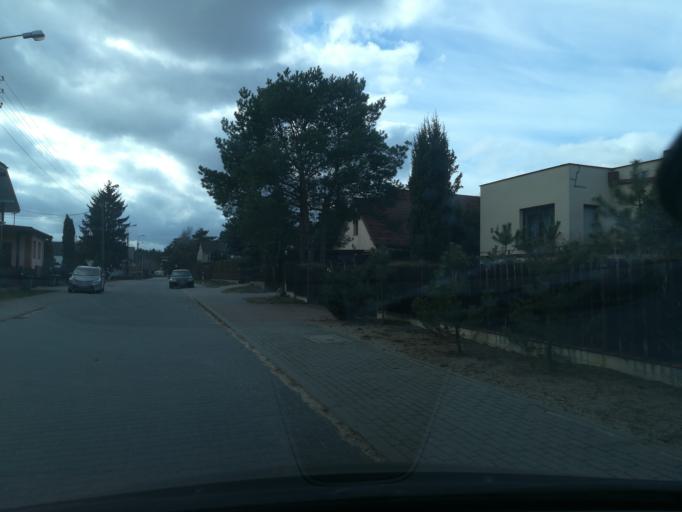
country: PL
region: Kujawsko-Pomorskie
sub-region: Powiat torunski
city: Lubicz Dolny
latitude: 52.9742
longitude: 18.6816
